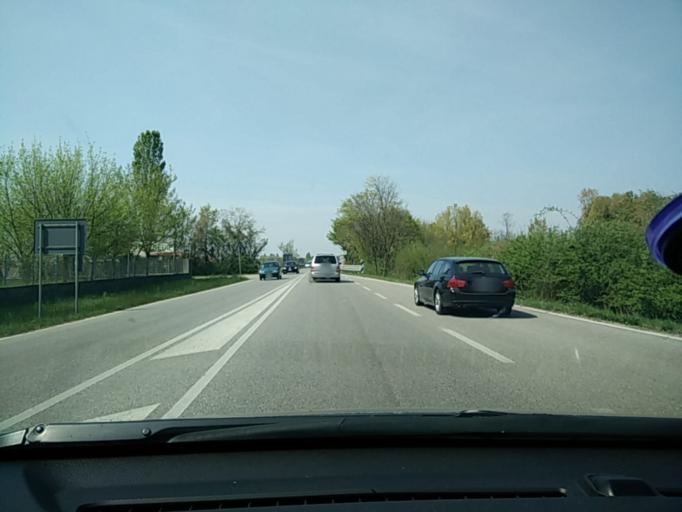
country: IT
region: Friuli Venezia Giulia
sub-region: Provincia di Udine
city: Buttrio
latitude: 45.9966
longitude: 13.3535
